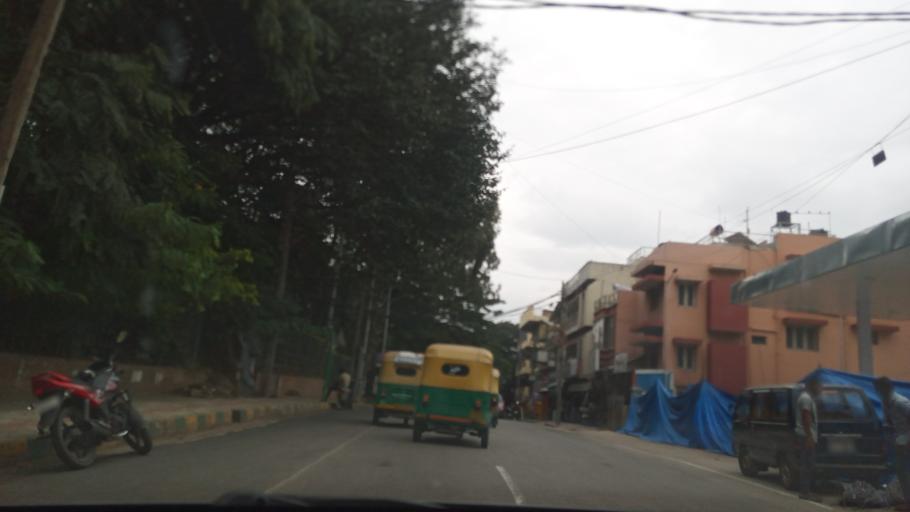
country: IN
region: Karnataka
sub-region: Bangalore Urban
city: Bangalore
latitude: 13.0082
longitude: 77.5458
